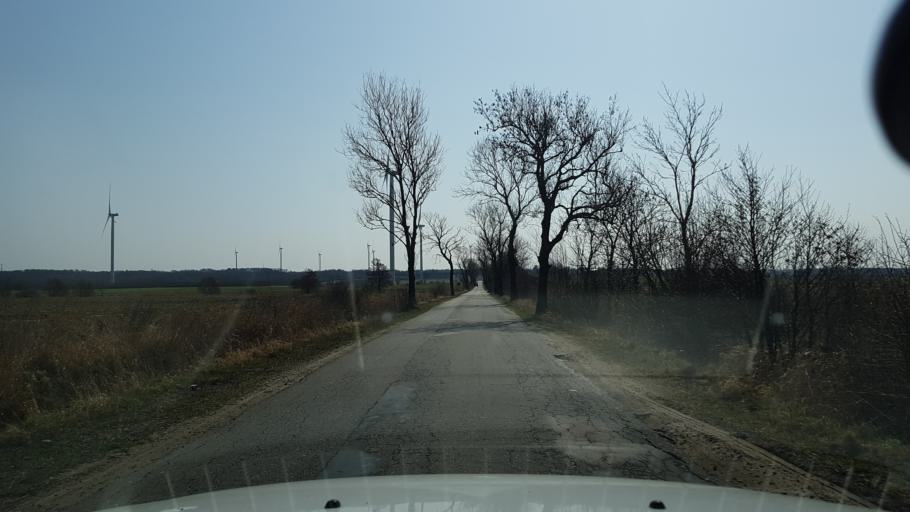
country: PL
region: West Pomeranian Voivodeship
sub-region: Powiat slawienski
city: Darlowo
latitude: 54.4955
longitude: 16.5037
